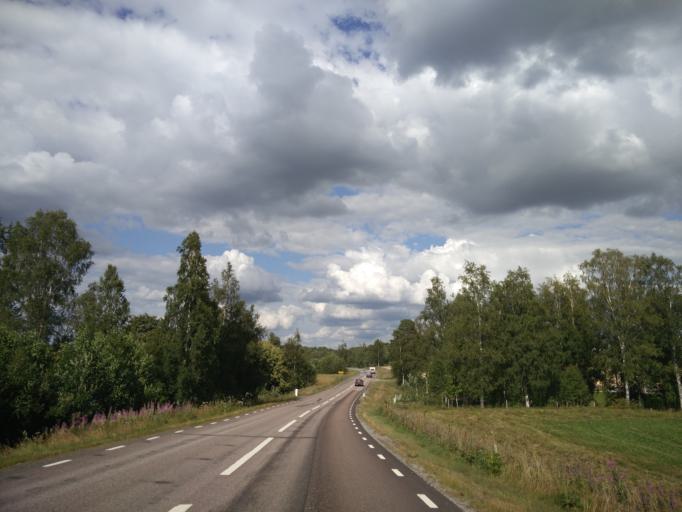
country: SE
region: Vaermland
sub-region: Sunne Kommun
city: Sunne
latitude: 59.7208
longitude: 13.1135
